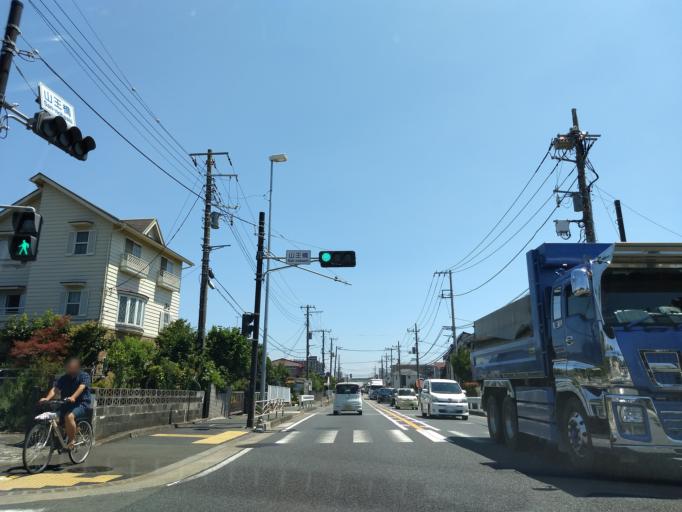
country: JP
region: Kanagawa
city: Isehara
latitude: 35.3935
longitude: 139.2862
